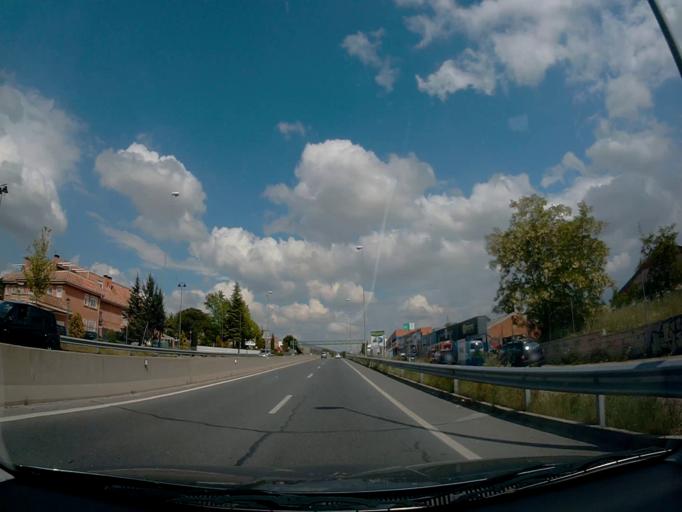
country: ES
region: Madrid
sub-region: Provincia de Madrid
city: Villaviciosa de Odon
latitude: 40.3520
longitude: -3.8889
